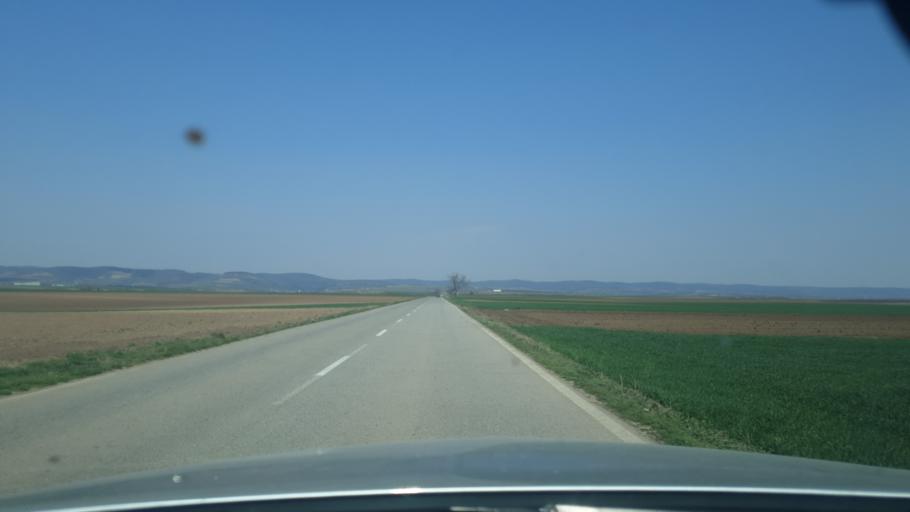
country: RS
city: Vrdnik
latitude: 45.0545
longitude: 19.7660
